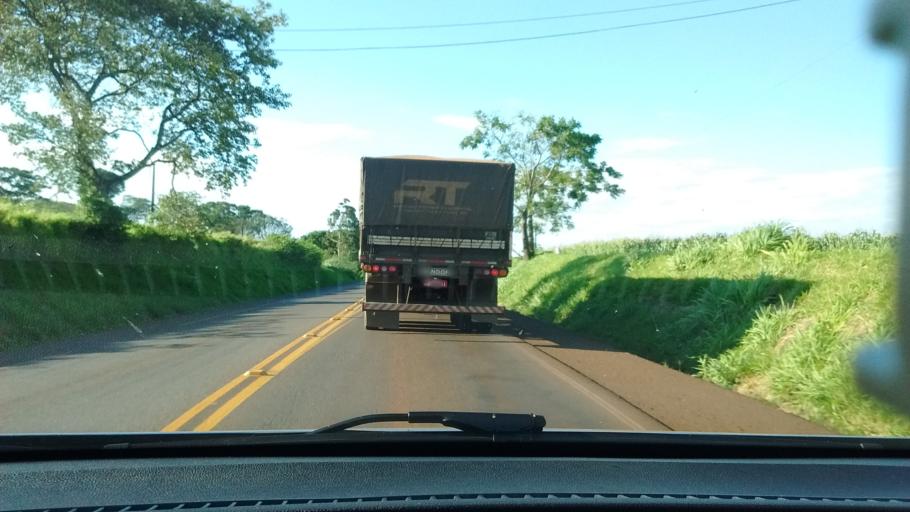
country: BR
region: Parana
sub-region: Cascavel
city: Cascavel
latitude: -25.2340
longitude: -53.5897
